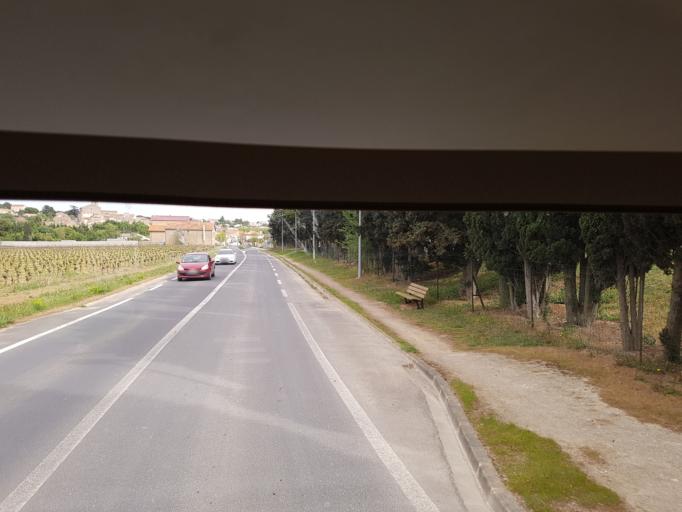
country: FR
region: Languedoc-Roussillon
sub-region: Departement de l'Herault
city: Vendres
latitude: 43.2699
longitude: 3.2175
